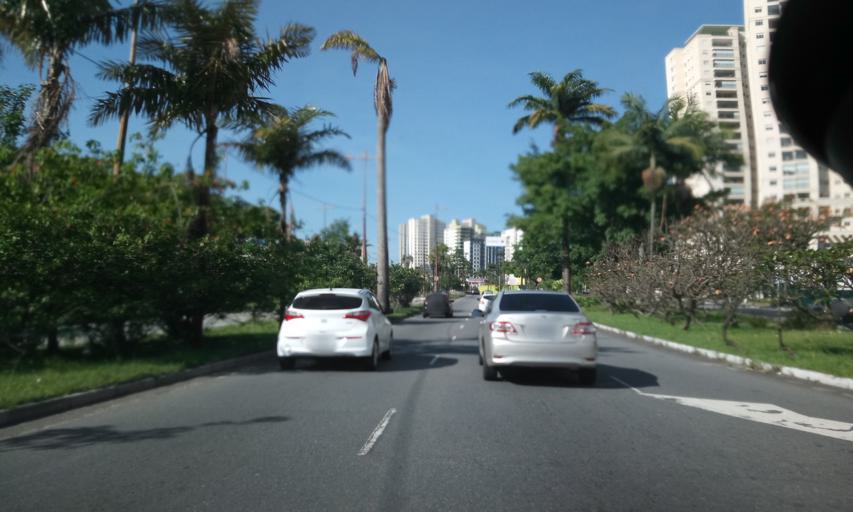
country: BR
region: Sao Paulo
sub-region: Santo Andre
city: Santo Andre
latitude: -23.6688
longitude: -46.5342
